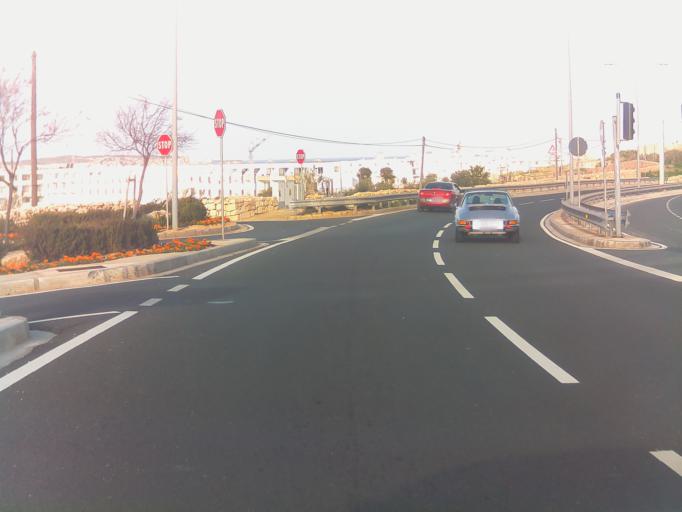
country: MT
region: Il-Mellieha
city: Mellieha
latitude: 35.9628
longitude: 14.3523
